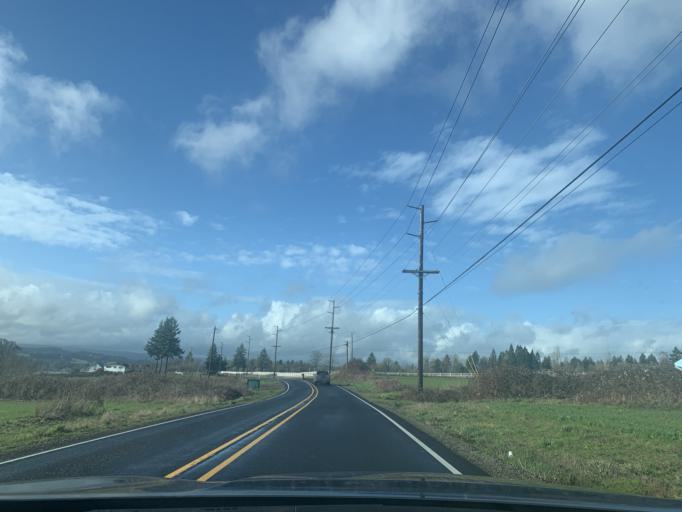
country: US
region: Oregon
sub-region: Washington County
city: King City
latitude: 45.4018
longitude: -122.8349
